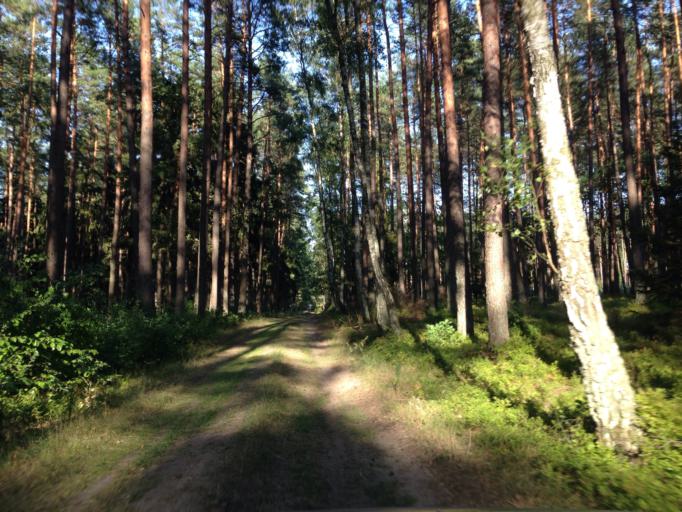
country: PL
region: Kujawsko-Pomorskie
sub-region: Powiat brodnicki
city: Gorzno
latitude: 53.1927
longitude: 19.7124
